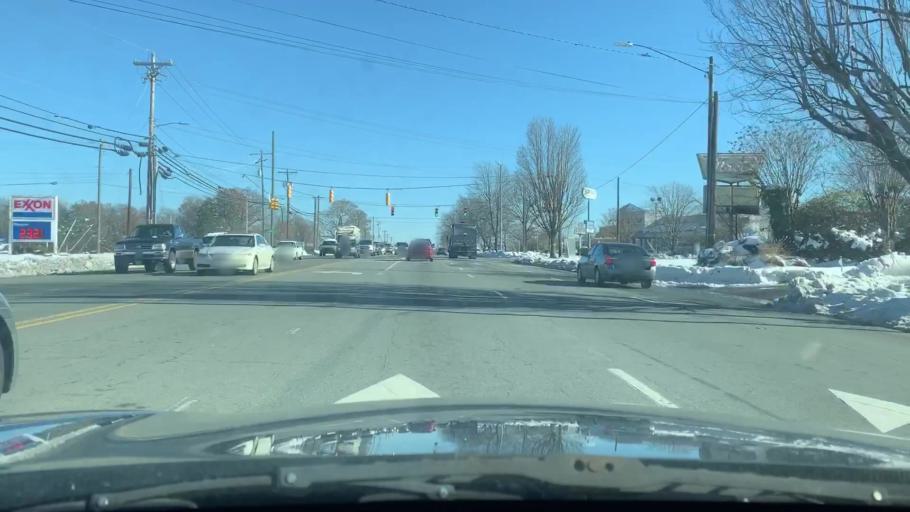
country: US
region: North Carolina
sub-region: Alamance County
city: Graham
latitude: 36.0955
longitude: -79.4068
